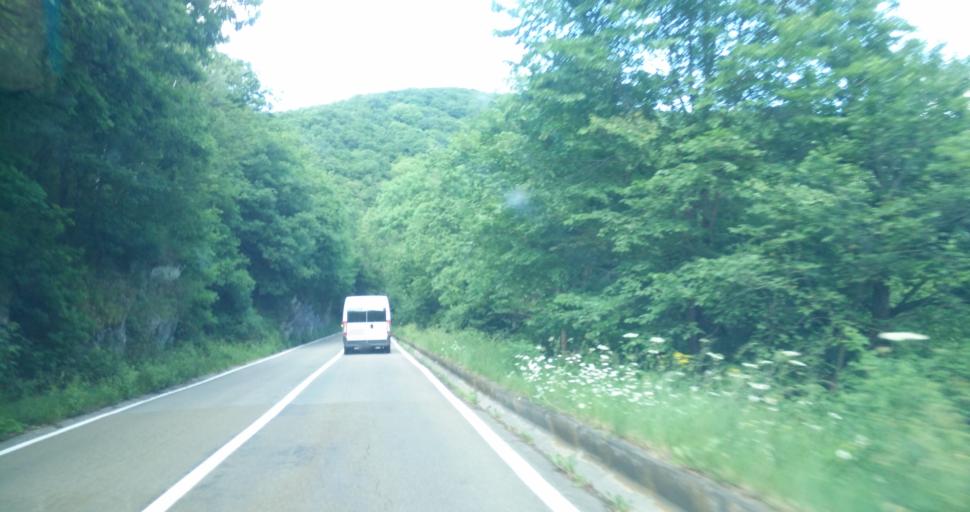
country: BE
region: Wallonia
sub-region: Province du Luxembourg
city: La Roche-en-Ardenne
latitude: 50.1746
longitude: 5.6072
